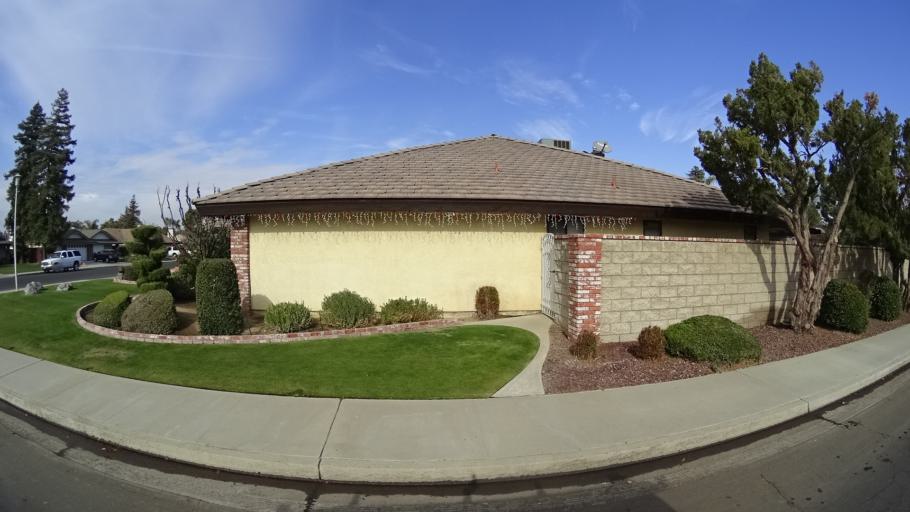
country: US
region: California
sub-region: Kern County
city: Greenacres
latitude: 35.4065
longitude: -119.0799
